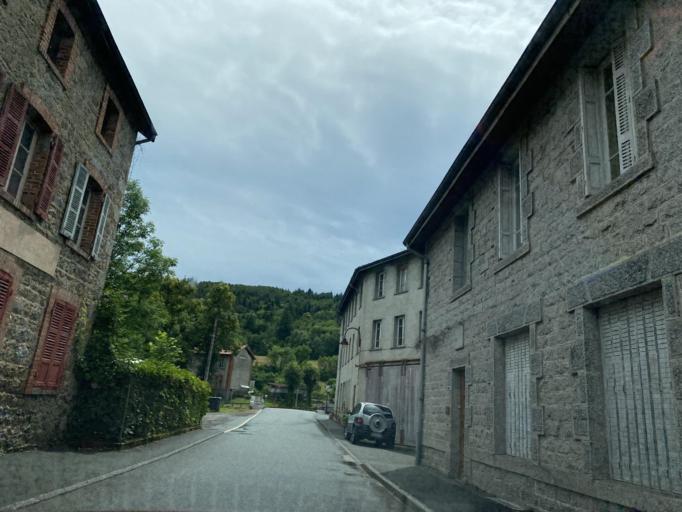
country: FR
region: Rhone-Alpes
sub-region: Departement de la Loire
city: Noiretable
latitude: 45.8137
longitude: 3.8258
